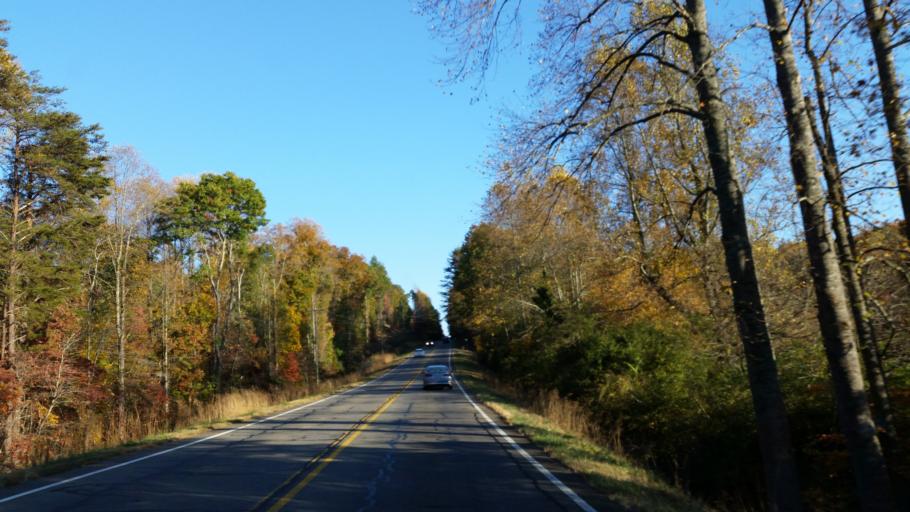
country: US
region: Georgia
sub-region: Pickens County
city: Jasper
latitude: 34.5992
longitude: -84.3336
